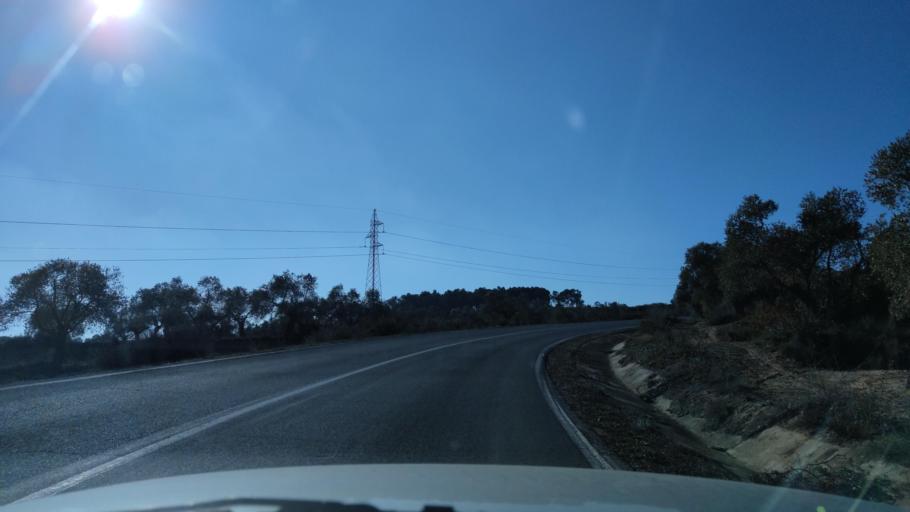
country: ES
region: Catalonia
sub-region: Provincia de Lleida
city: Maials
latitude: 41.3368
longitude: 0.4601
